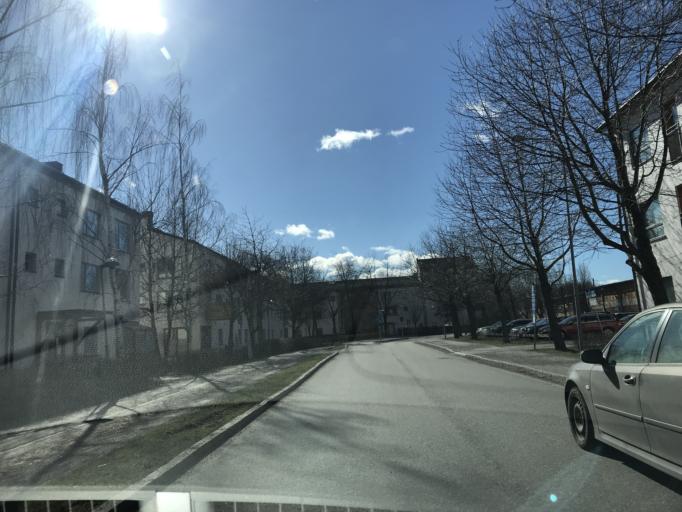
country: SE
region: Stockholm
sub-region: Stockholms Kommun
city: Kista
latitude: 59.3962
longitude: 17.9420
